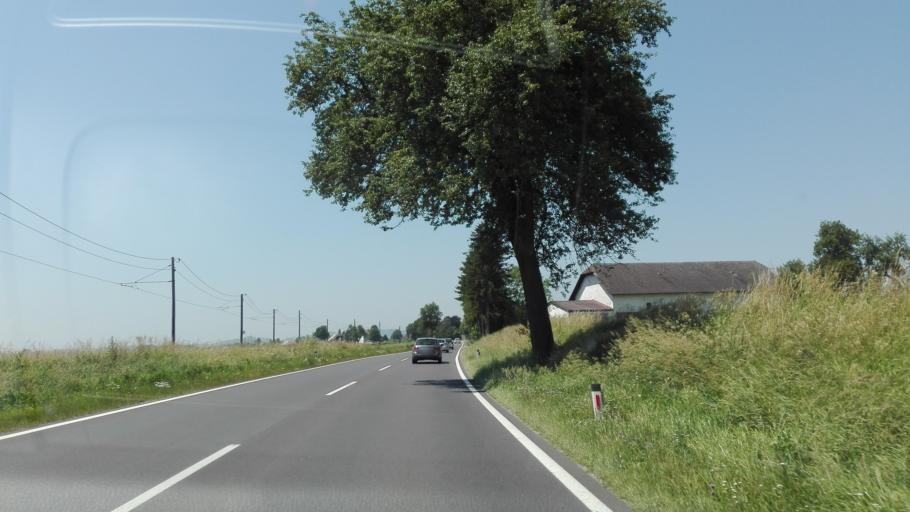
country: AT
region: Upper Austria
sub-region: Politischer Bezirk Urfahr-Umgebung
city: Goldworth
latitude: 48.2863
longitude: 14.0907
